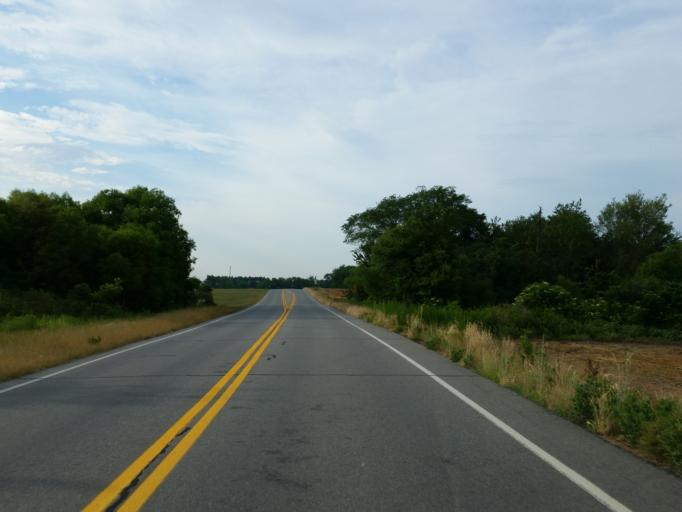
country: US
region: Georgia
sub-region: Dooly County
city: Unadilla
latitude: 32.1806
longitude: -83.7646
